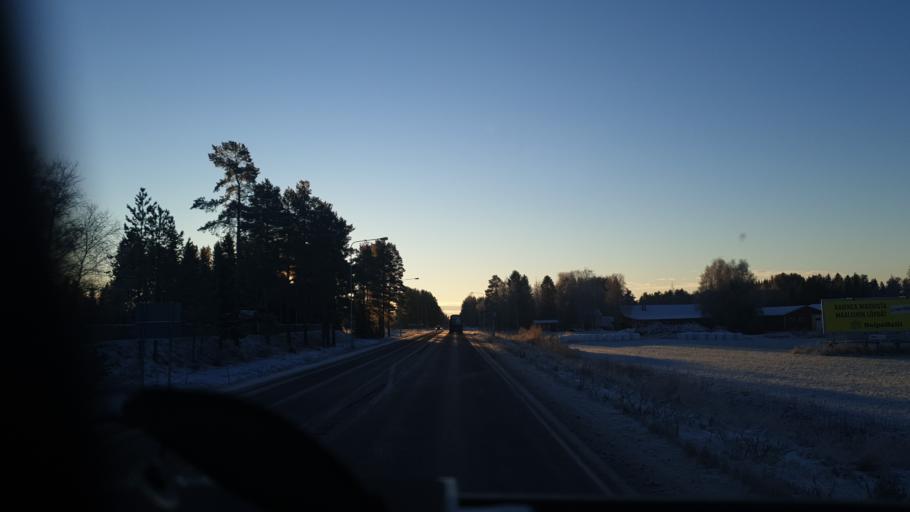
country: FI
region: Northern Ostrobothnia
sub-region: Ylivieska
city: Kalajoki
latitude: 64.2802
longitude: 23.9485
